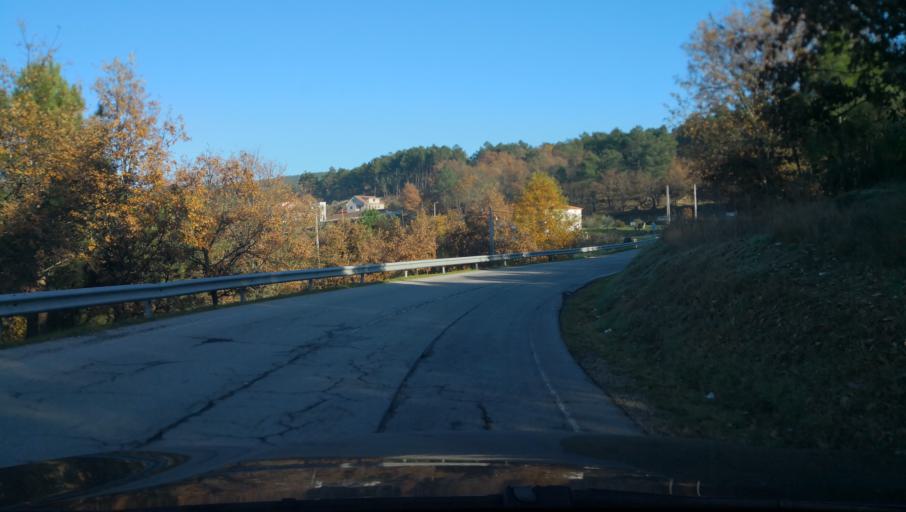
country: PT
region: Vila Real
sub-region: Vila Real
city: Vila Real
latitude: 41.3296
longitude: -7.6704
